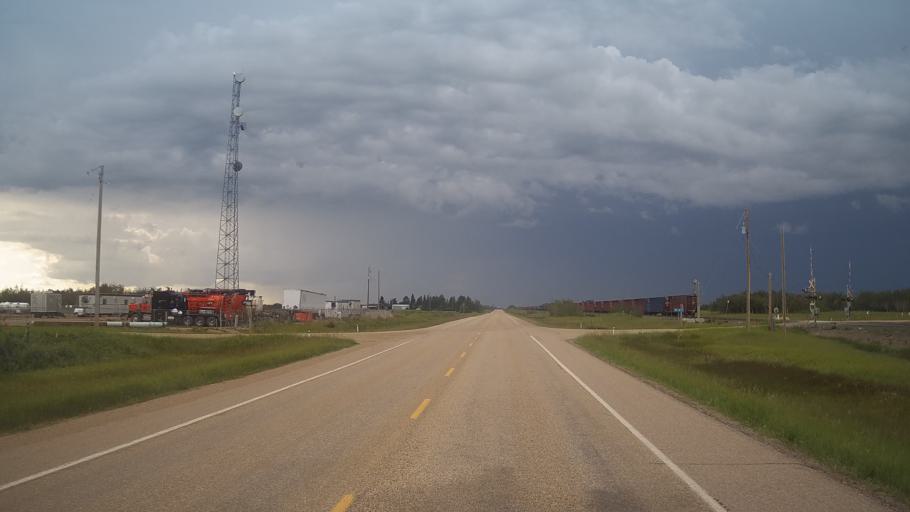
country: CA
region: Alberta
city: Tofield
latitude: 53.2689
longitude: -112.3668
